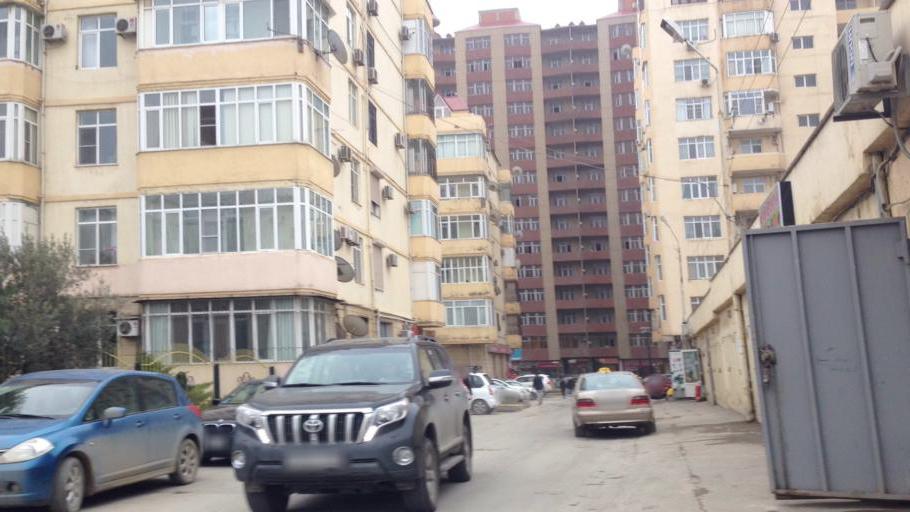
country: AZ
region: Baki
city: Baku
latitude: 40.3850
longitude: 49.8703
